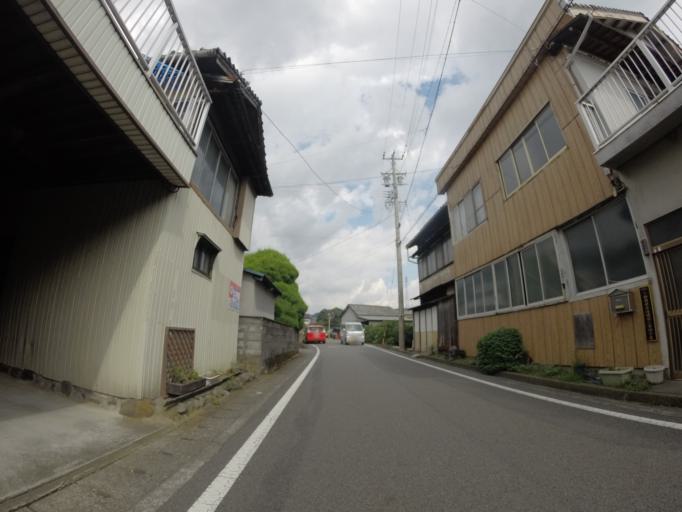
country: JP
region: Shizuoka
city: Shizuoka-shi
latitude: 35.0534
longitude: 138.4760
